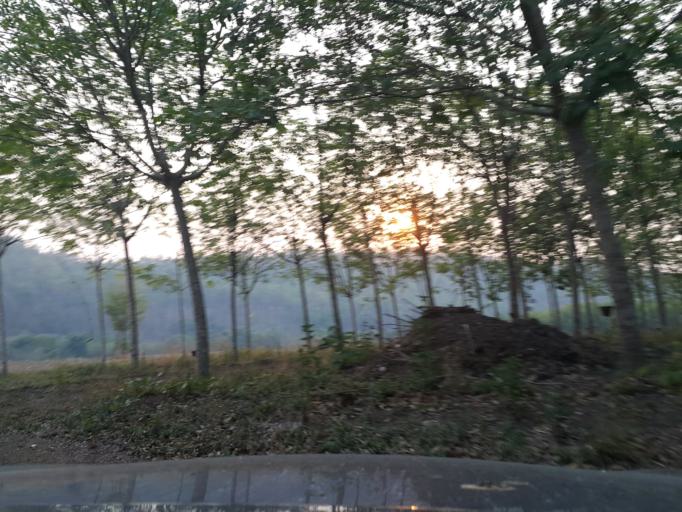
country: TH
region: Lamphun
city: Thung Hua Chang
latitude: 17.9169
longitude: 99.0726
